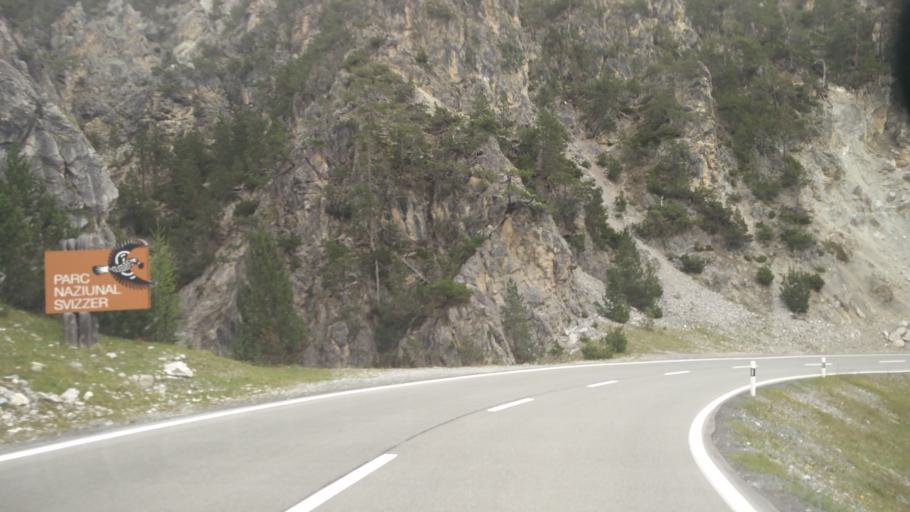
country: CH
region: Grisons
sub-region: Inn District
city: Zernez
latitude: 46.6806
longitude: 10.1654
